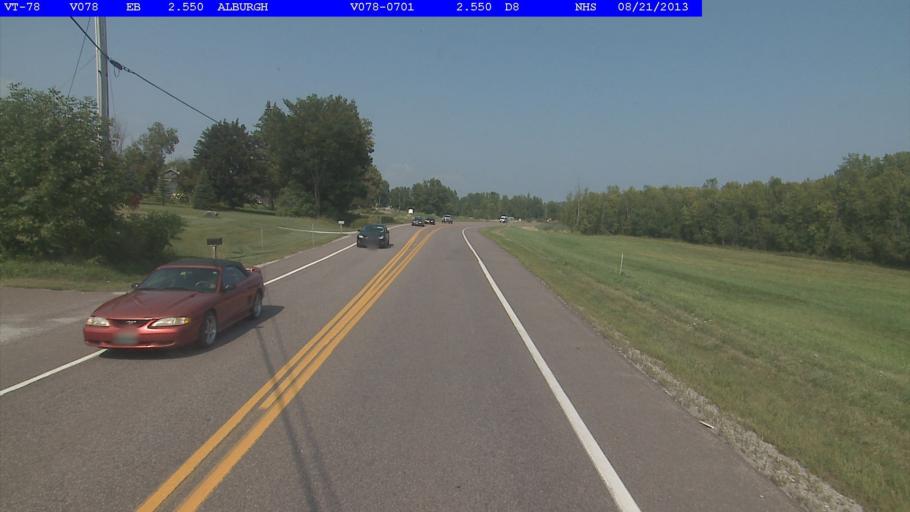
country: US
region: Vermont
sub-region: Franklin County
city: Swanton
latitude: 44.9729
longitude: -73.2340
